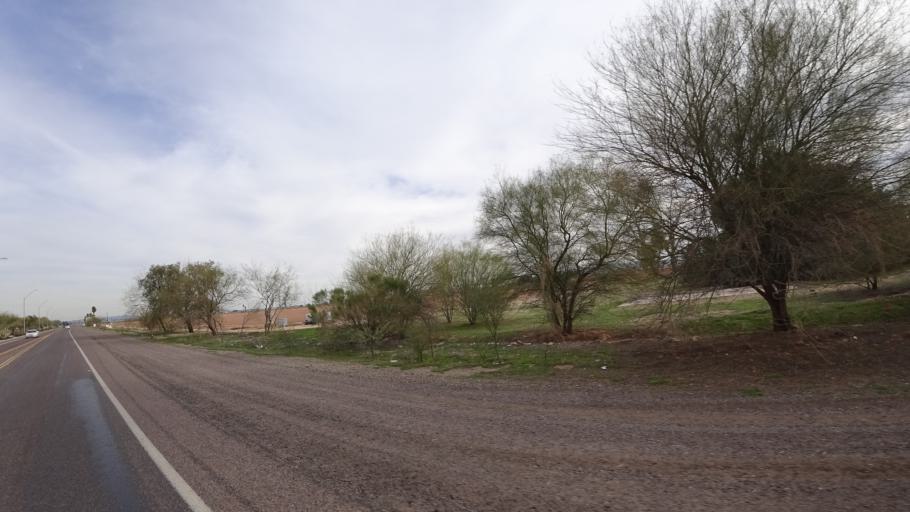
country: US
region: Arizona
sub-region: Maricopa County
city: El Mirage
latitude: 33.5803
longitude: -112.3665
